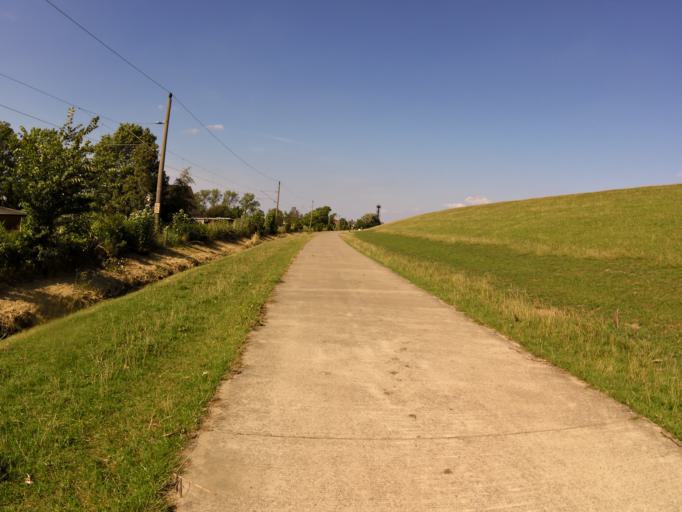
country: DE
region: Lower Saxony
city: Nordenham
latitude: 53.4613
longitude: 8.4750
